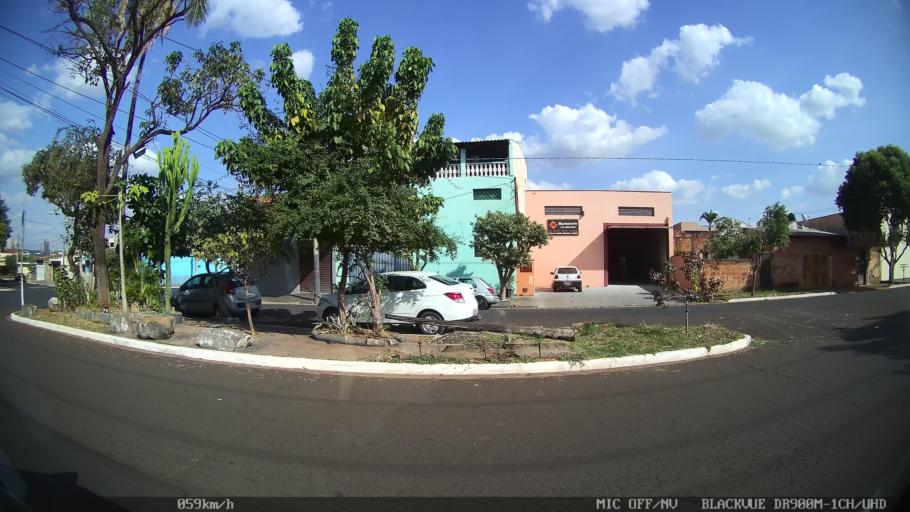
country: BR
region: Sao Paulo
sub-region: Ribeirao Preto
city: Ribeirao Preto
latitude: -21.1969
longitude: -47.8358
